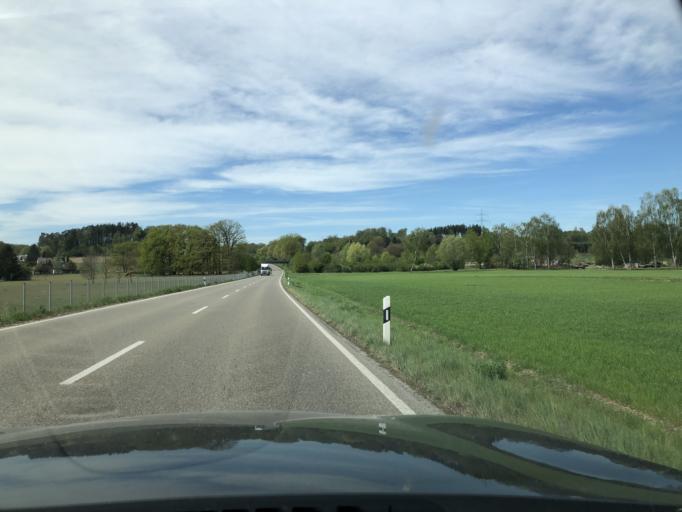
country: DE
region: Bavaria
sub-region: Swabia
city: Biberbach
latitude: 48.5244
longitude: 10.8187
